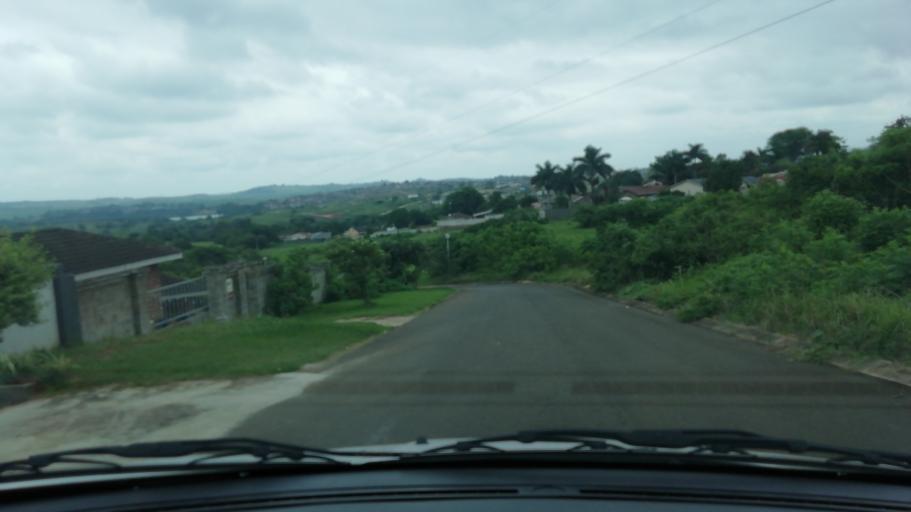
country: ZA
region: KwaZulu-Natal
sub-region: uThungulu District Municipality
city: Empangeni
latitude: -28.7591
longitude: 31.8844
